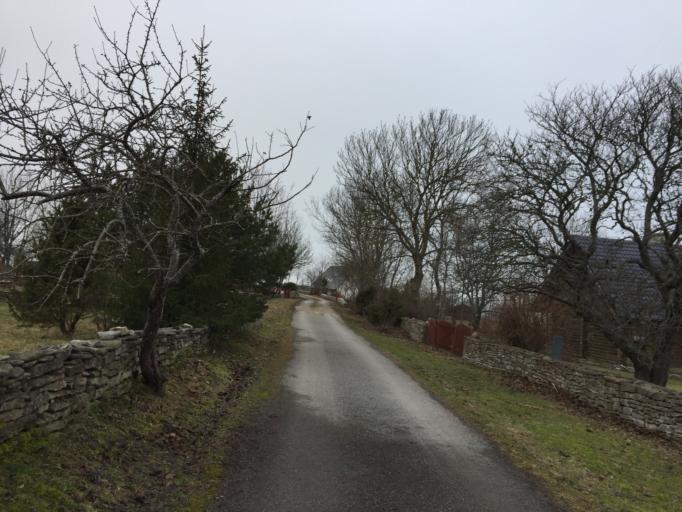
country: EE
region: Saare
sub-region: Kuressaare linn
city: Kuressaare
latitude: 58.5450
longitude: 22.2168
